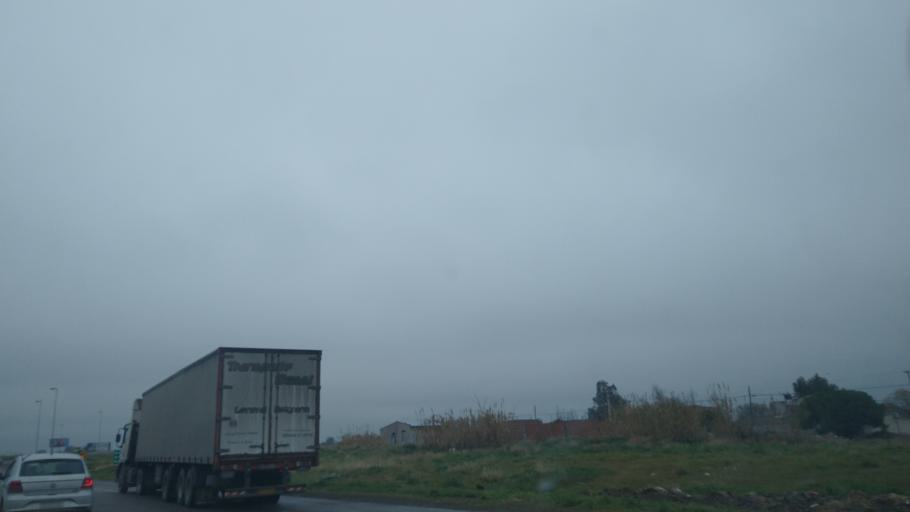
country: AR
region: Buenos Aires
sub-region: Partido de Bahia Blanca
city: Bahia Blanca
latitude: -38.7451
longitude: -62.2324
